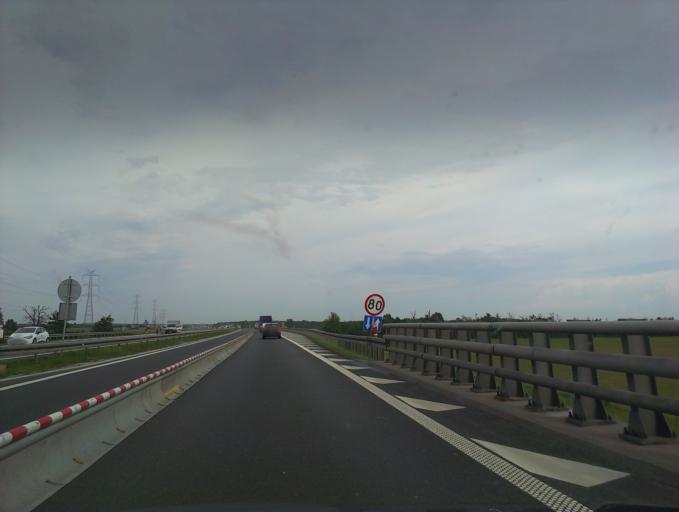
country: PL
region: Opole Voivodeship
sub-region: Powiat brzeski
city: Losiow
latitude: 50.7246
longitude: 17.5209
